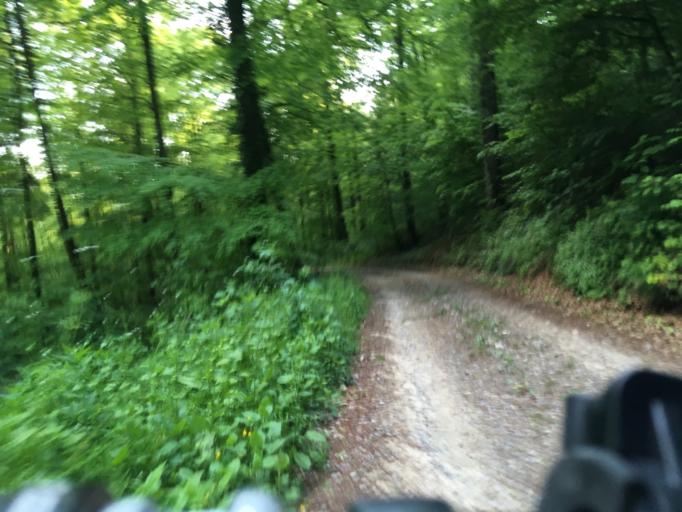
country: CH
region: Schaffhausen
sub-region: Bezirk Stein
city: Ramsen
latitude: 47.7021
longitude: 8.7944
